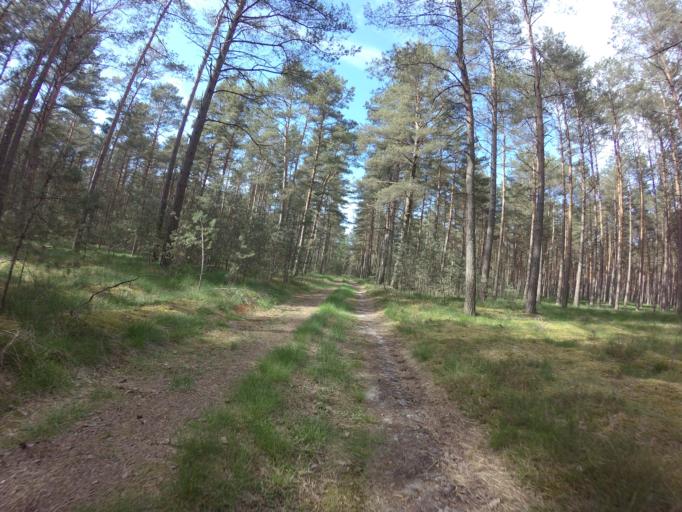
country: PL
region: West Pomeranian Voivodeship
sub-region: Powiat choszczenski
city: Drawno
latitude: 53.1919
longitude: 15.7347
